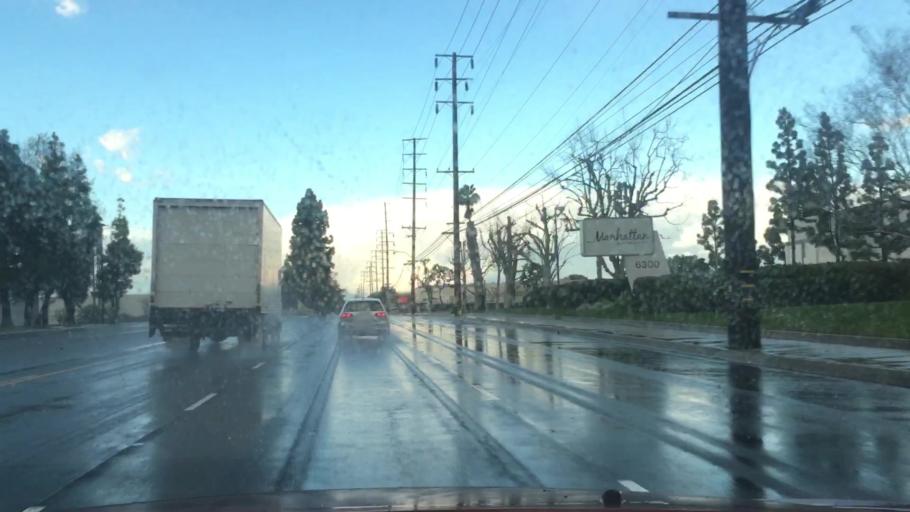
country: US
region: California
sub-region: Orange County
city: La Palma
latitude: 33.8699
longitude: -118.0287
